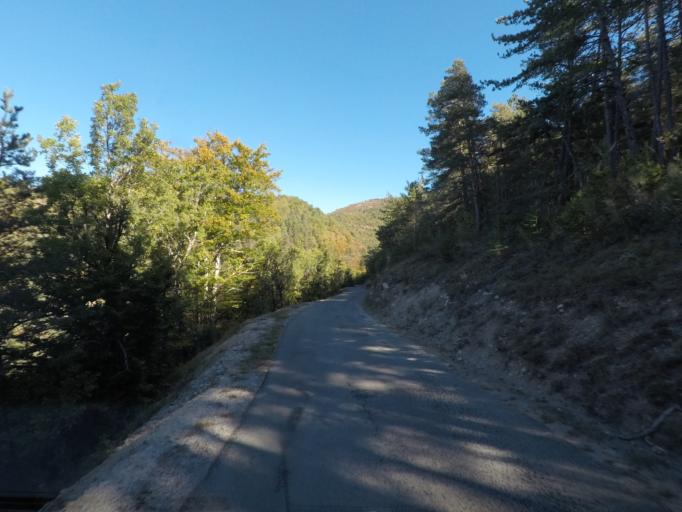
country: FR
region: Rhone-Alpes
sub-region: Departement de la Drome
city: Die
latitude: 44.5548
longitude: 5.3569
